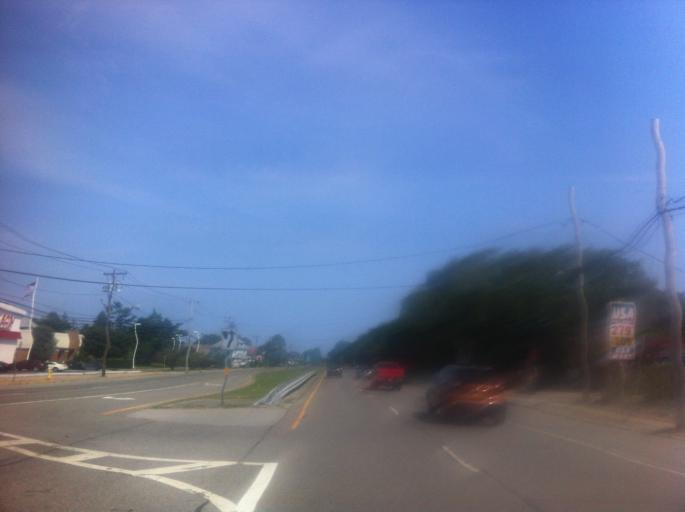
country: US
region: New York
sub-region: Suffolk County
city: West Babylon
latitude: 40.7091
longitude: -73.3565
